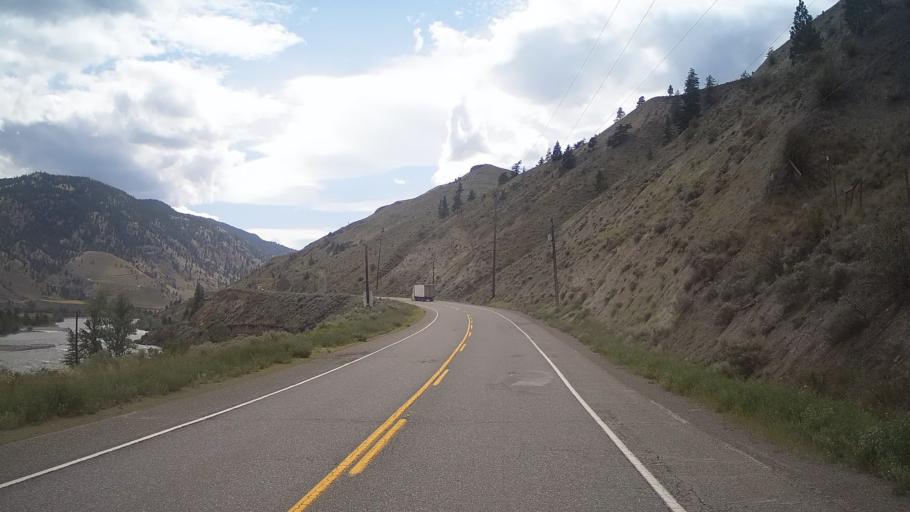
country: CA
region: British Columbia
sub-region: Thompson-Nicola Regional District
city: Ashcroft
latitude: 50.4822
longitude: -121.3019
